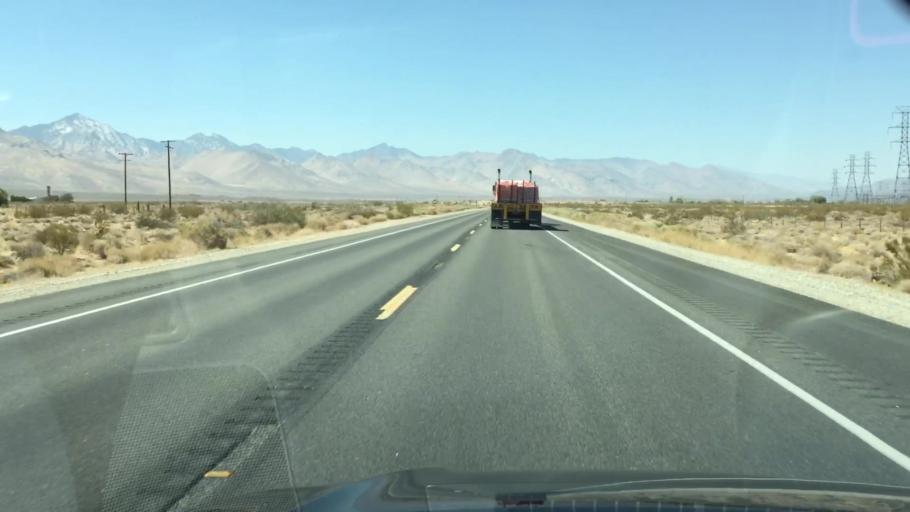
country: US
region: California
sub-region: Kern County
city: Inyokern
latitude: 35.6427
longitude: -117.7931
